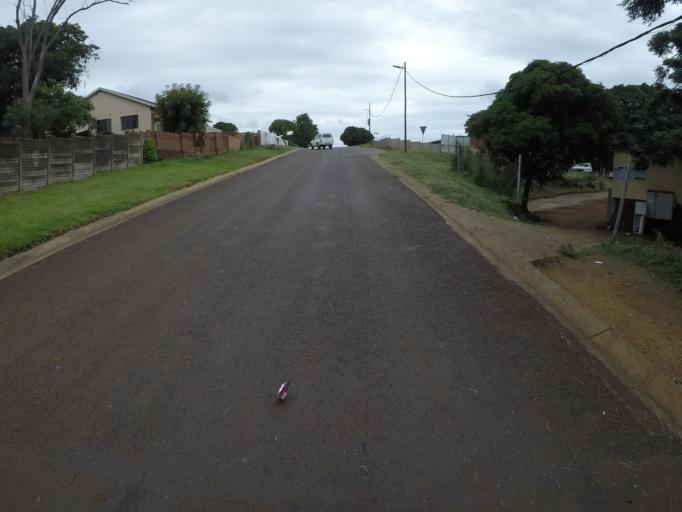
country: ZA
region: KwaZulu-Natal
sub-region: uThungulu District Municipality
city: Empangeni
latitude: -28.7717
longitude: 31.8614
